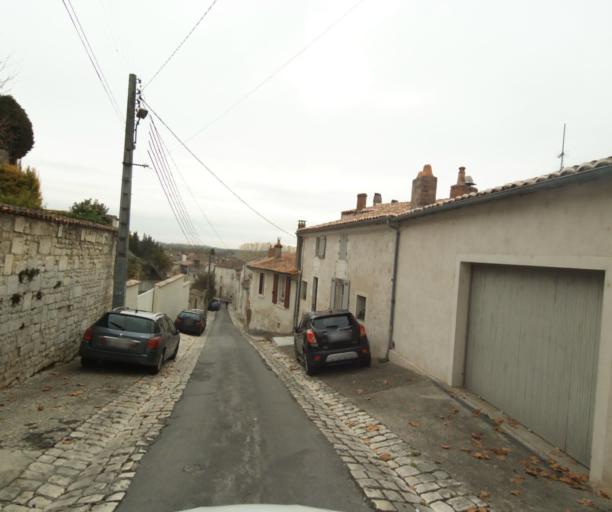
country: FR
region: Poitou-Charentes
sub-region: Departement de la Charente-Maritime
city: Saintes
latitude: 45.7443
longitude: -0.6382
